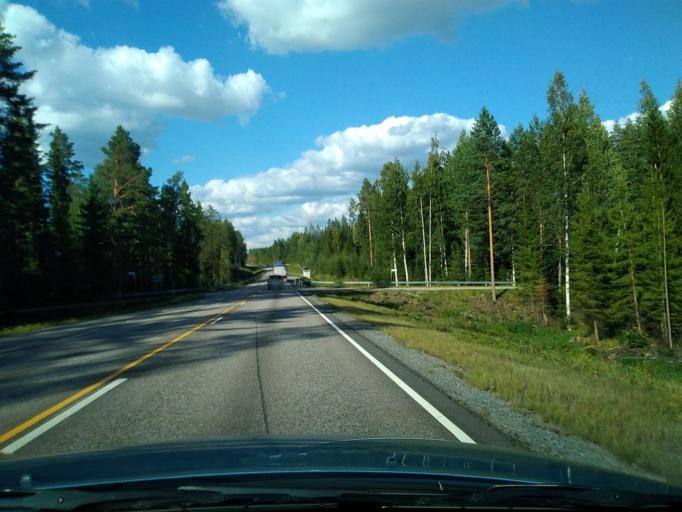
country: FI
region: Central Finland
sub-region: Keuruu
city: Keuruu
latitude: 62.1372
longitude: 24.7407
